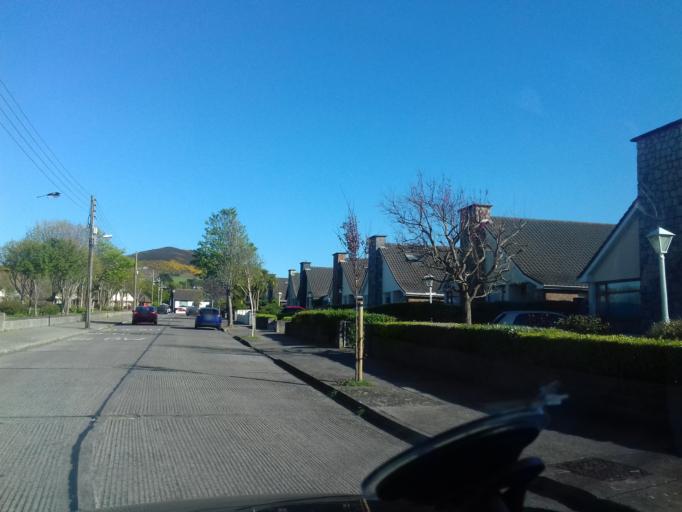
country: IE
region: Leinster
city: Sutton
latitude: 53.3806
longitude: -6.0987
